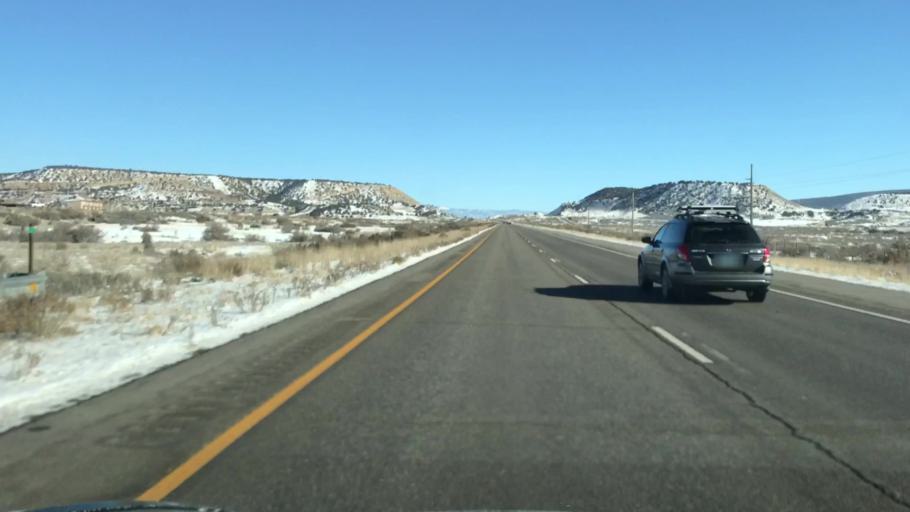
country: US
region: Colorado
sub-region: Garfield County
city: Rifle
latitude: 39.5028
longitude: -107.9012
